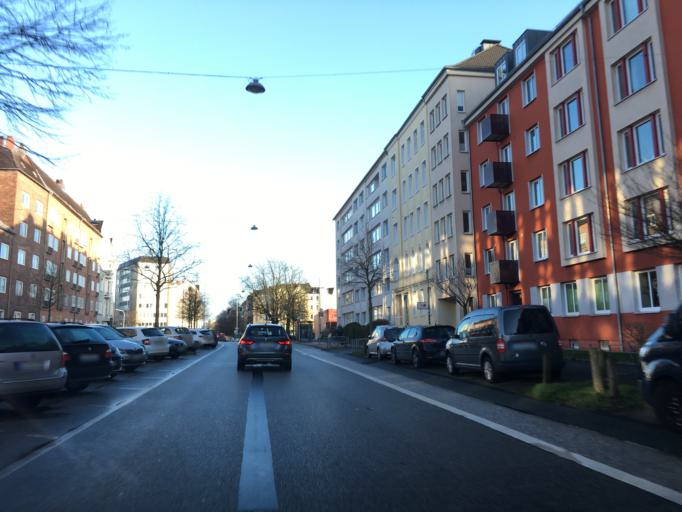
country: DE
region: Schleswig-Holstein
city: Kiel
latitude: 54.3449
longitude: 10.1333
